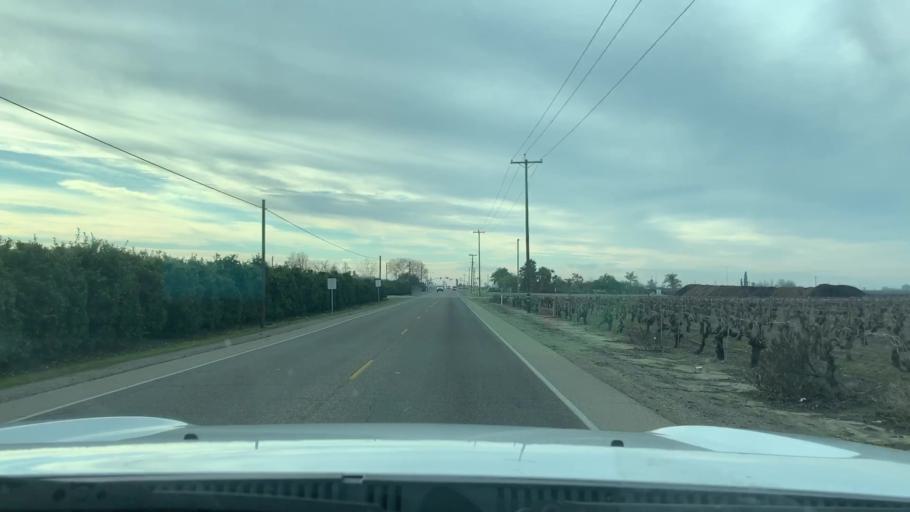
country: US
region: California
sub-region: Fresno County
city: Easton
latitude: 36.6053
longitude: -119.7803
